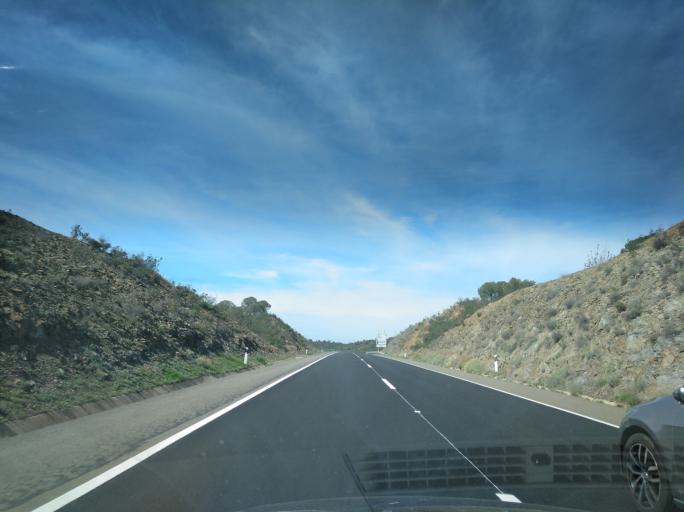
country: PT
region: Faro
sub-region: Alcoutim
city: Alcoutim
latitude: 37.3501
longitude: -7.5114
